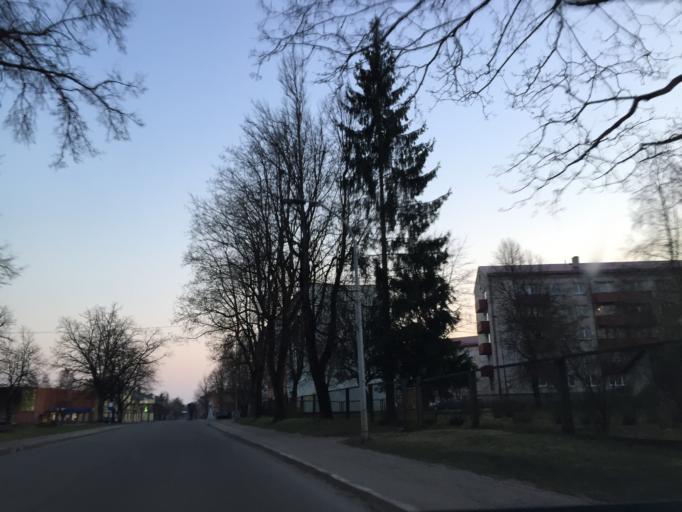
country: LV
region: Valkas Rajons
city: Valka
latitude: 57.7764
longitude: 26.0226
